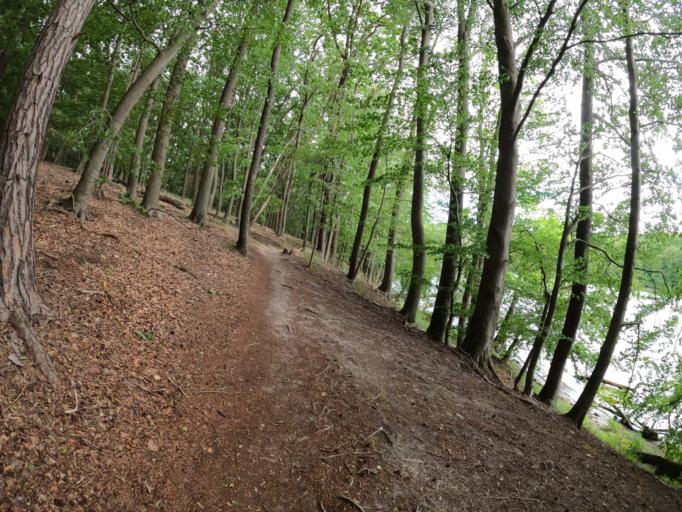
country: DE
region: Brandenburg
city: Angermunde
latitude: 53.0232
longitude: 13.9138
